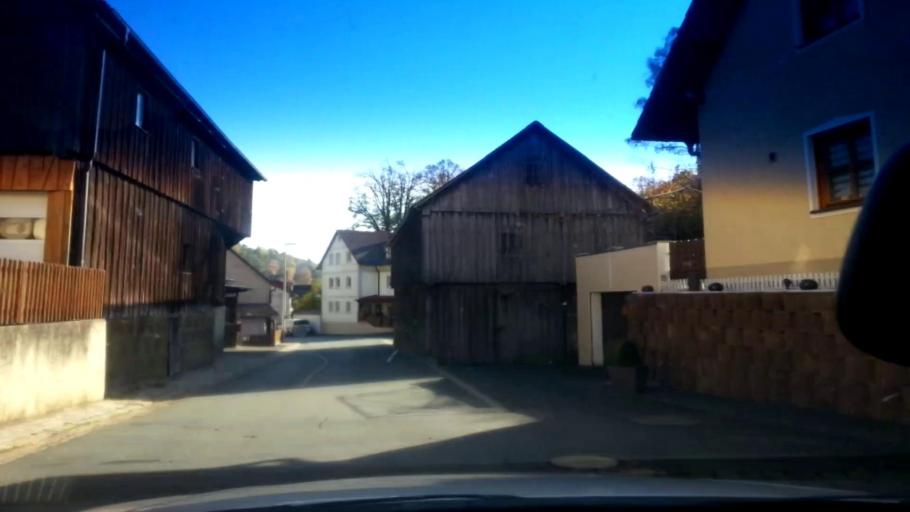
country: DE
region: Bavaria
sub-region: Upper Franconia
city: Wonsees
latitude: 49.9751
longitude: 11.2698
